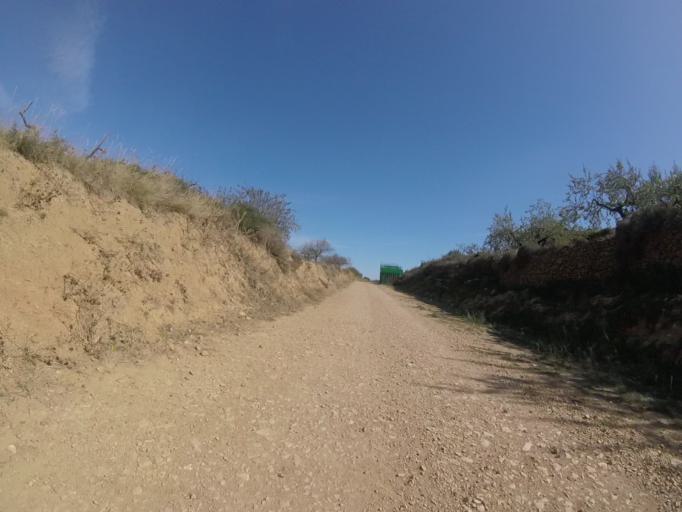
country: ES
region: Valencia
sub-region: Provincia de Castello
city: Sierra-Engarceran
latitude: 40.2735
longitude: -0.0069
